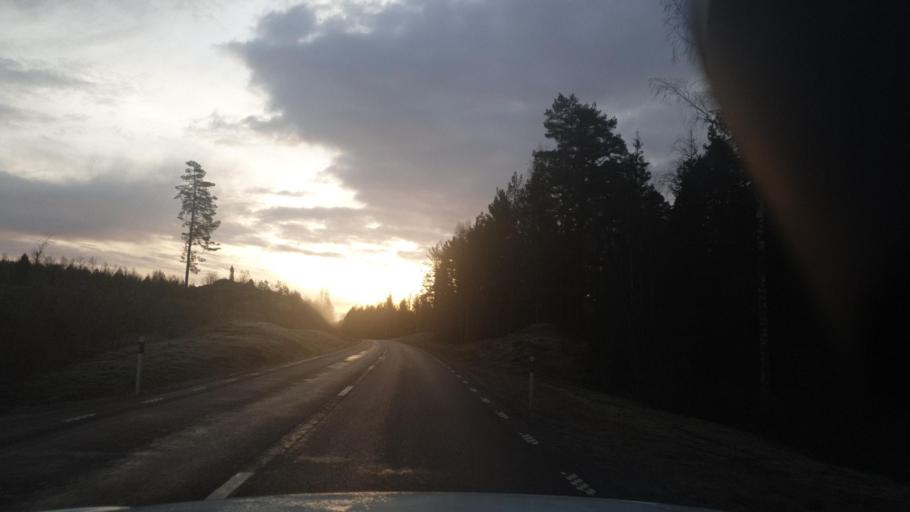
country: SE
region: Vaermland
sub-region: Arvika Kommun
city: Arvika
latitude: 59.5503
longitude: 12.7311
